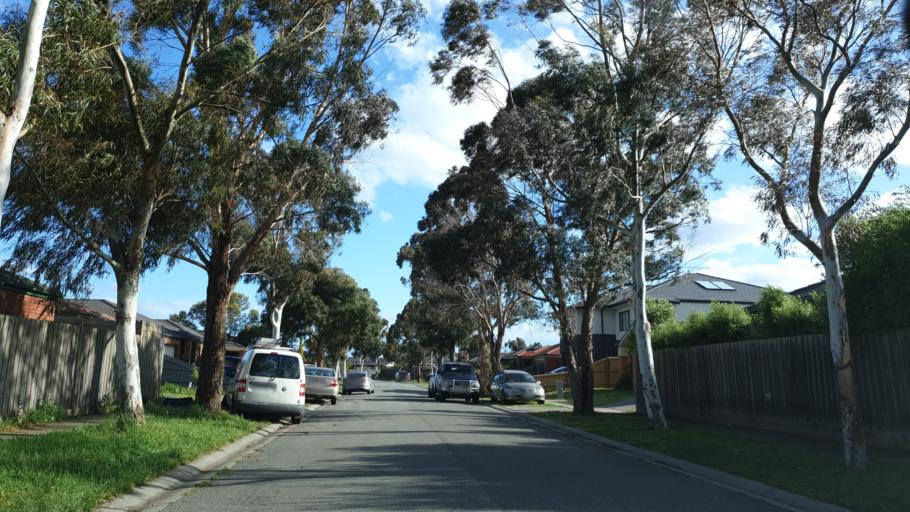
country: AU
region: Victoria
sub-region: Casey
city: Cranbourne
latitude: -38.0913
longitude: 145.2889
